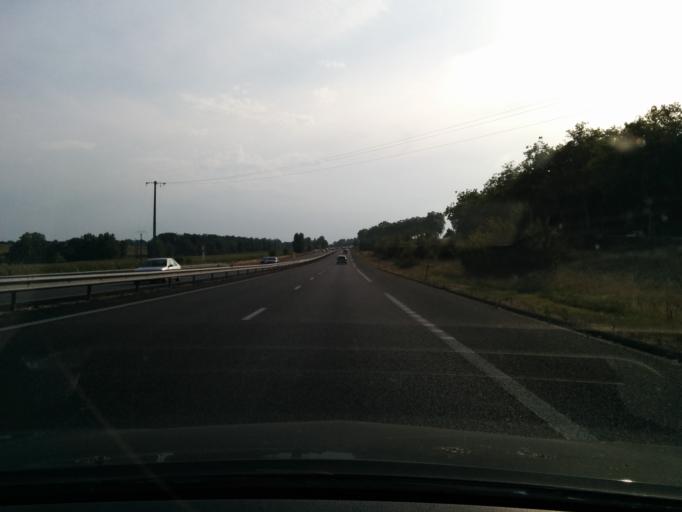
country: FR
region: Midi-Pyrenees
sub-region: Departement de la Haute-Garonne
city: Montastruc-la-Conseillere
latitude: 43.7450
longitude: 1.6060
